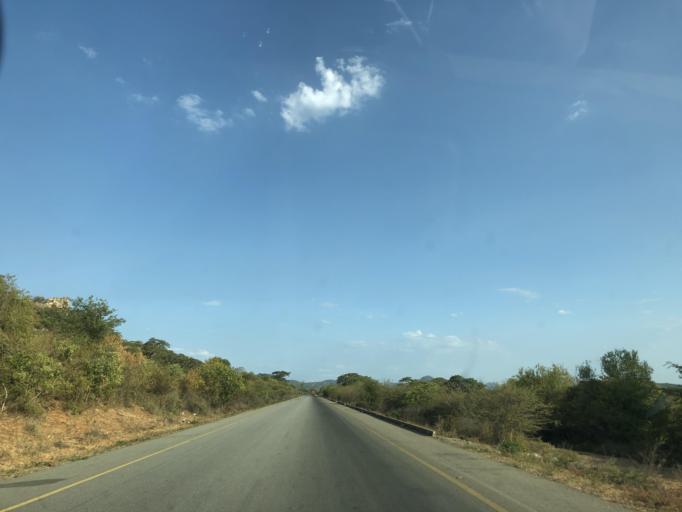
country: AO
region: Benguela
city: Benguela
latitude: -13.3607
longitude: 13.8549
